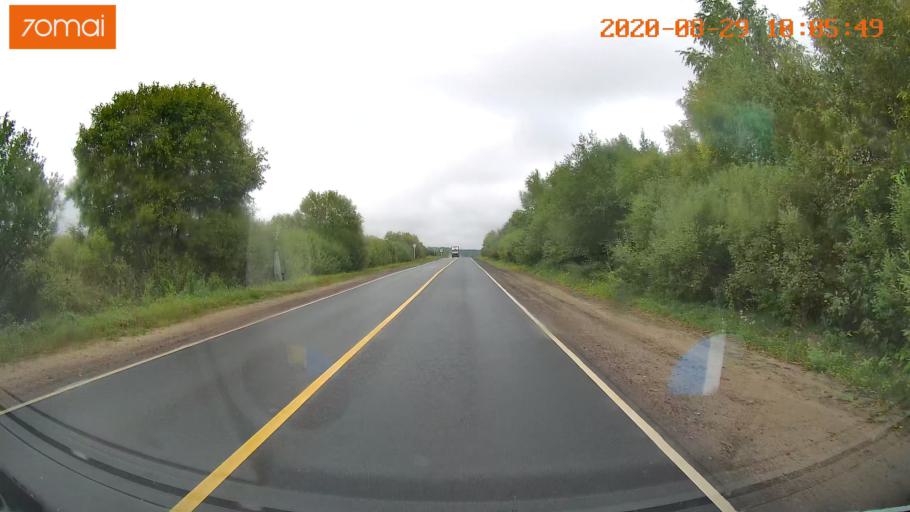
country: RU
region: Ivanovo
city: Zarechnyy
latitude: 57.3914
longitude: 42.5305
